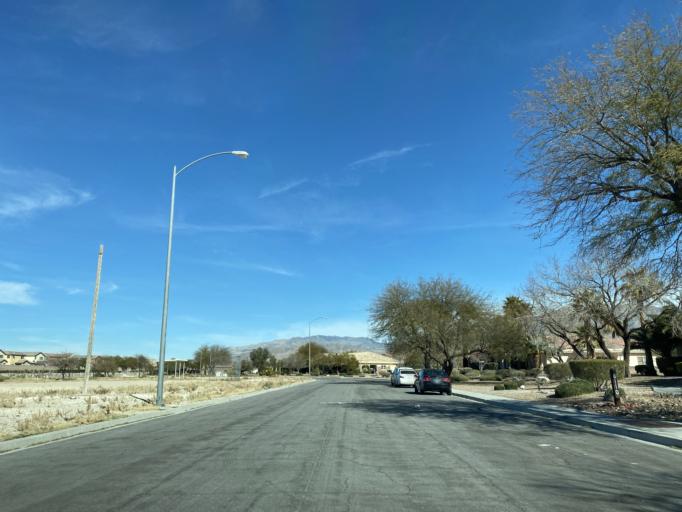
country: US
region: Nevada
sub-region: Clark County
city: North Las Vegas
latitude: 36.3070
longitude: -115.2409
